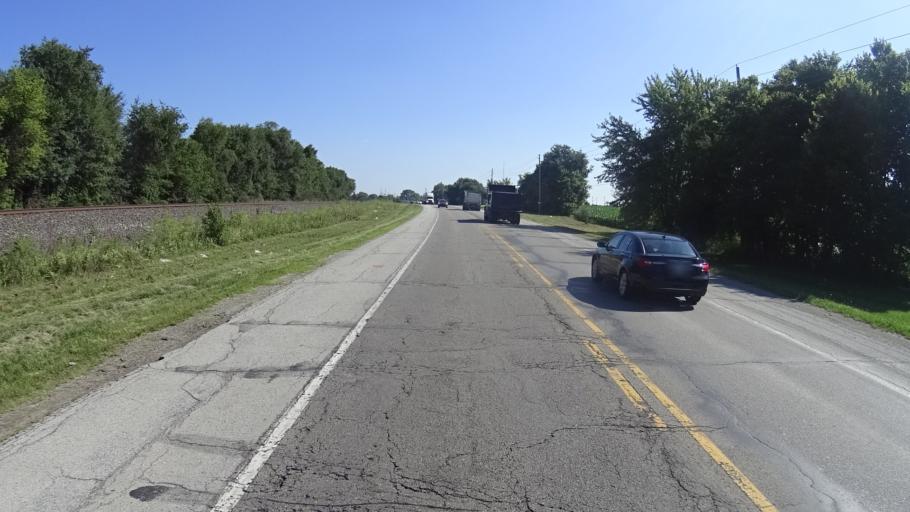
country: US
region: Indiana
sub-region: Madison County
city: Pendleton
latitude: 39.9910
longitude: -85.7406
